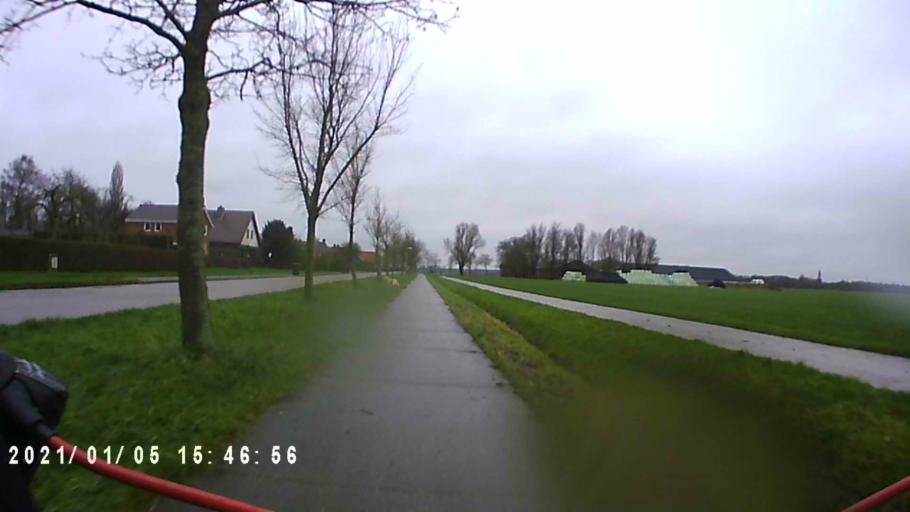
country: NL
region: Groningen
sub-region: Gemeente  Oldambt
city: Winschoten
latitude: 53.2044
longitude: 7.1155
